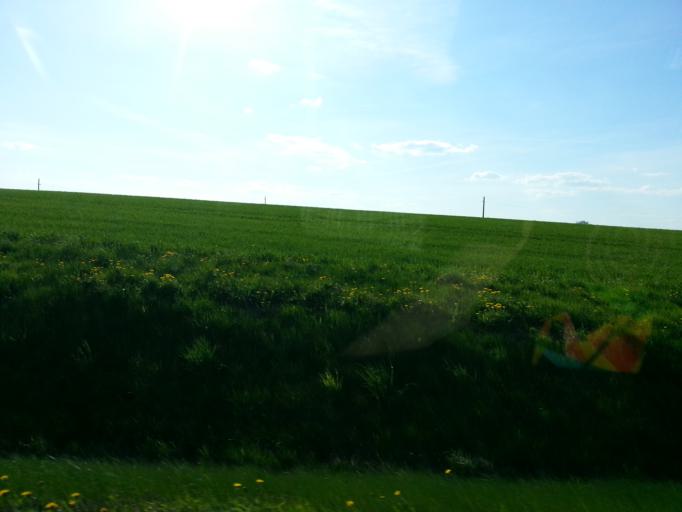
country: LT
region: Panevezys
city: Pasvalys
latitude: 55.9881
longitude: 24.3429
